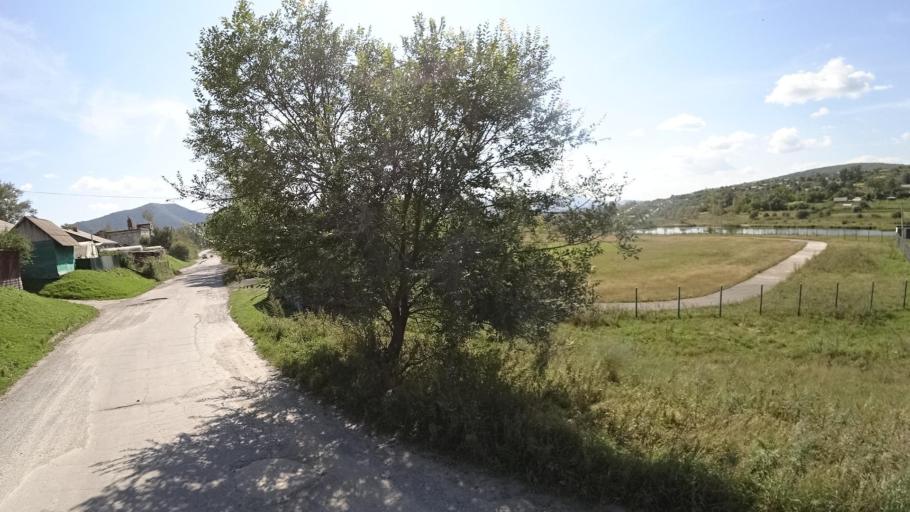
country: RU
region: Jewish Autonomous Oblast
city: Londoko
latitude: 49.0074
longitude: 131.8793
